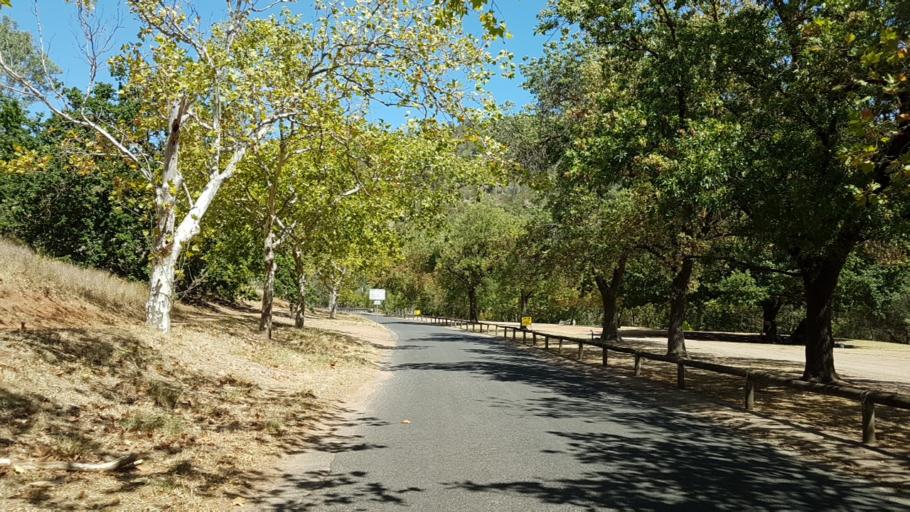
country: AU
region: South Australia
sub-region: Mitcham
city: Mitcham
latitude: -34.9886
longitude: 138.6286
